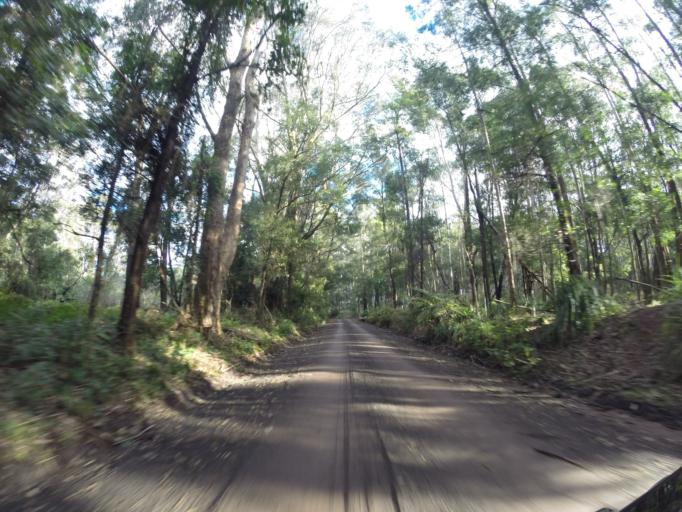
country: AU
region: New South Wales
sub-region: Wollongong
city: Cordeaux Heights
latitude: -34.4241
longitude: 150.7816
